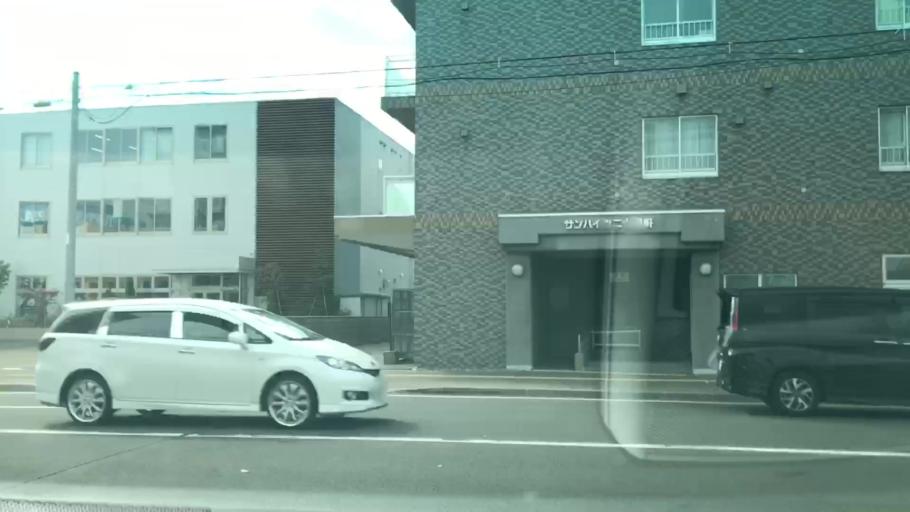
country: JP
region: Hokkaido
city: Sapporo
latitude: 43.0776
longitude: 141.3105
